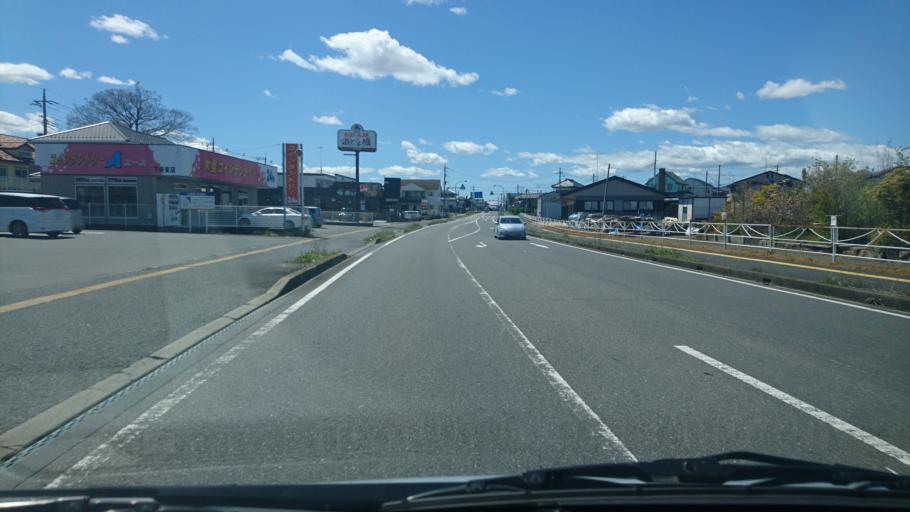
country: JP
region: Ibaraki
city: Ishige
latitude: 36.1878
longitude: 139.9690
